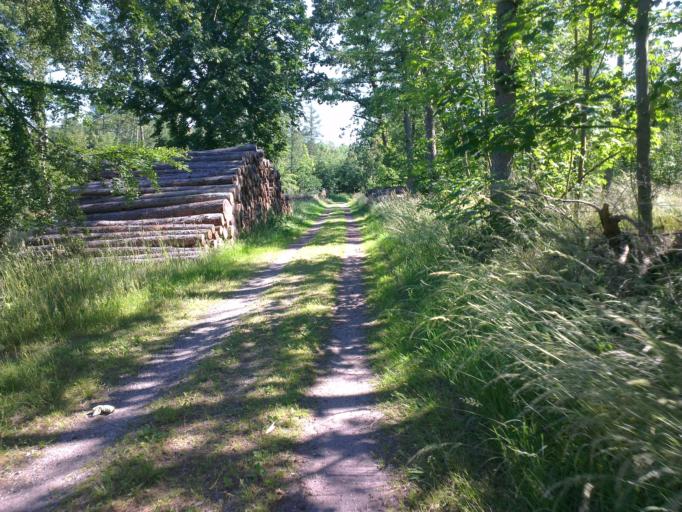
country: DK
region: Capital Region
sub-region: Frederikssund Kommune
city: Skibby
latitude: 55.7937
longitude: 11.8681
